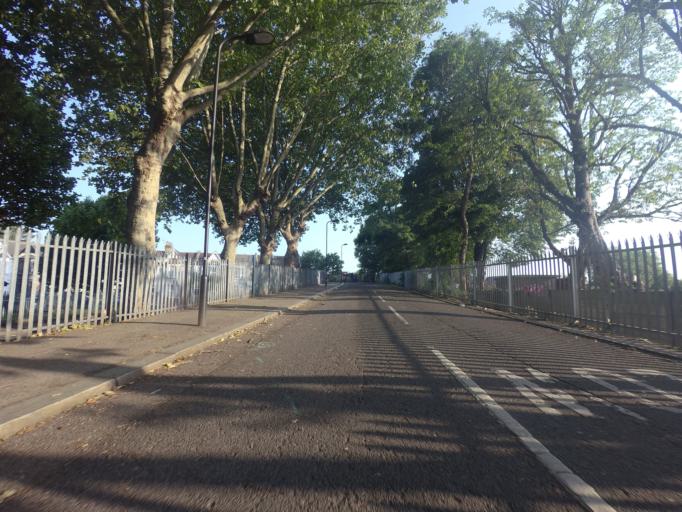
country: GB
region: England
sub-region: Greater London
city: Walthamstow
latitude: 51.5569
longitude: -0.0032
